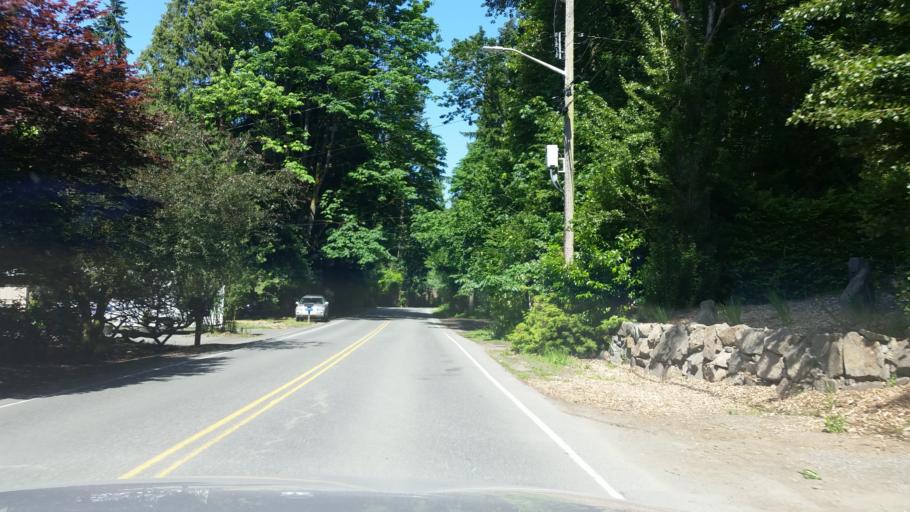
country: US
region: Washington
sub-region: King County
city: Lake Forest Park
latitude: 47.7568
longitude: -122.2884
